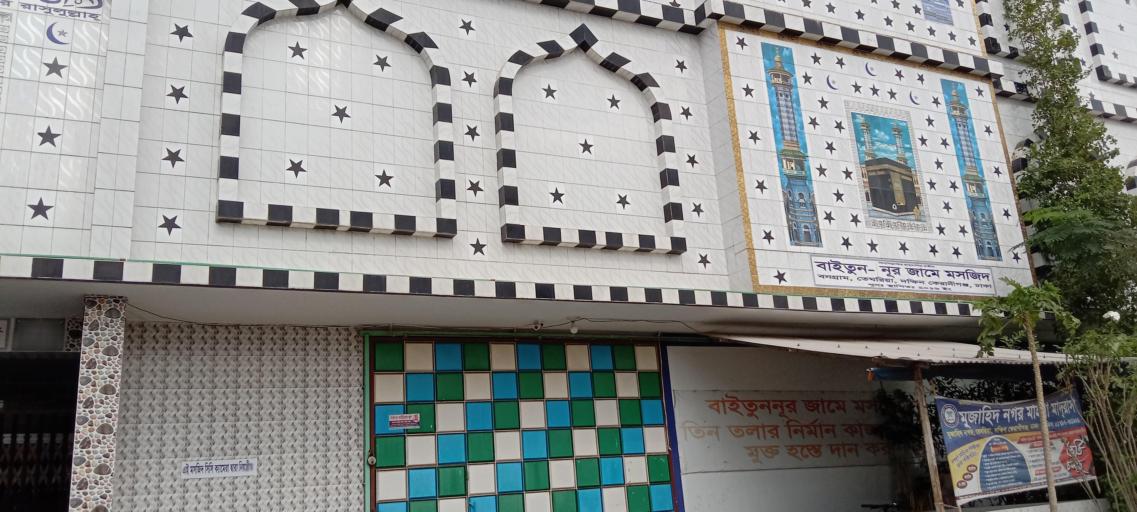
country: BD
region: Dhaka
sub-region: Dhaka
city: Dhaka
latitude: 23.6573
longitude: 90.4153
